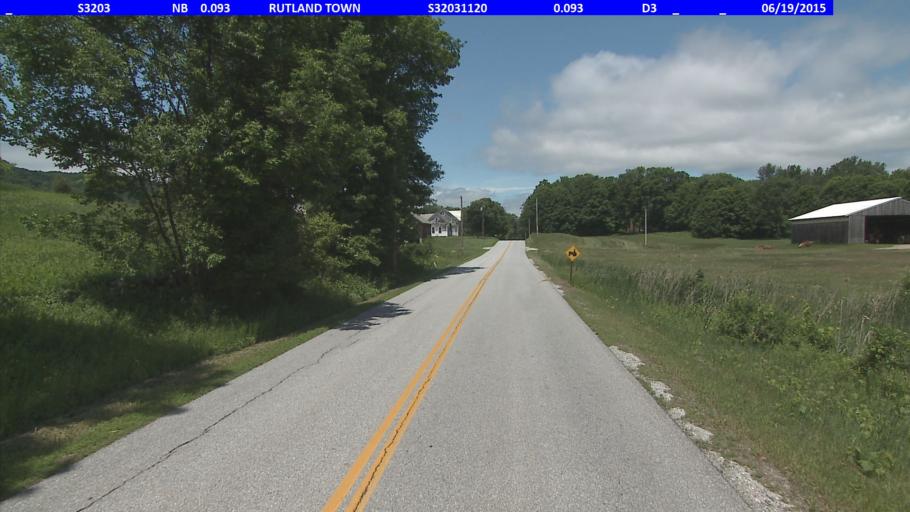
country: US
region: Vermont
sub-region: Rutland County
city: Rutland
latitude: 43.6550
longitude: -72.9963
